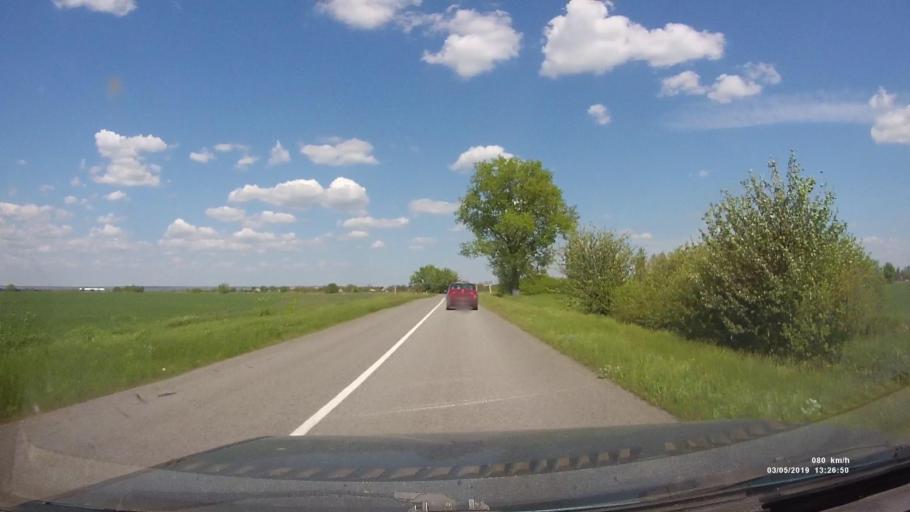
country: RU
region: Rostov
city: Semikarakorsk
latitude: 47.5740
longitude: 40.8259
